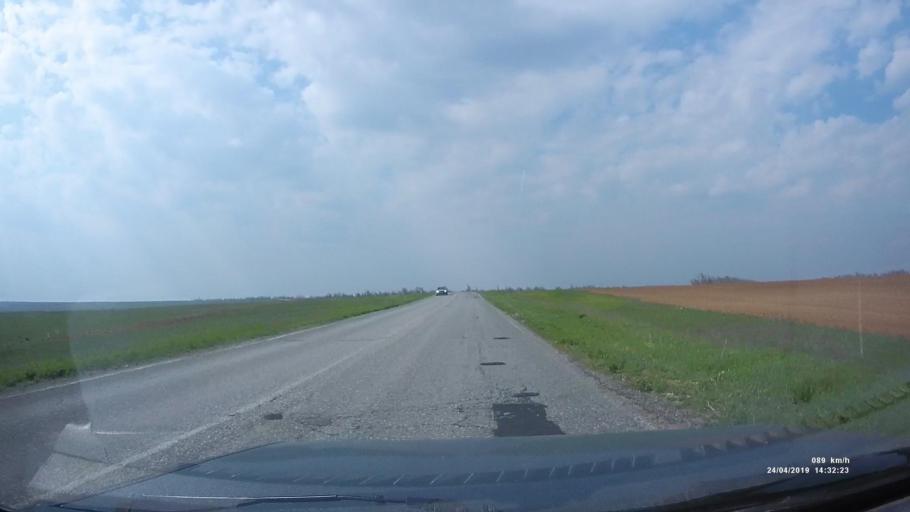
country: RU
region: Kalmykiya
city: Arshan'
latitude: 46.3652
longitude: 43.9677
